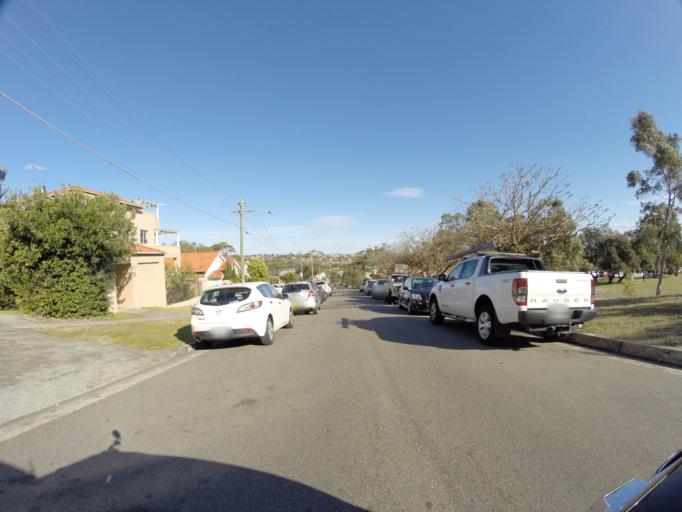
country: AU
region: New South Wales
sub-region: Randwick
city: Coogee
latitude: -33.9263
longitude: 151.2482
